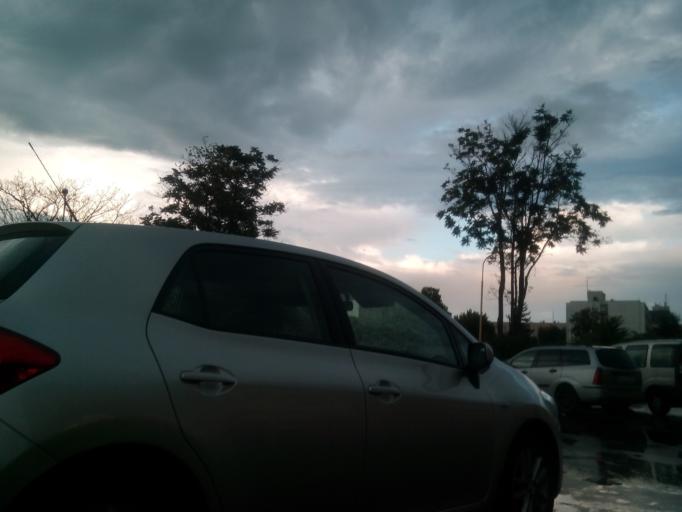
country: SK
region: Kosicky
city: Kosice
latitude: 48.7325
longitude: 21.2607
